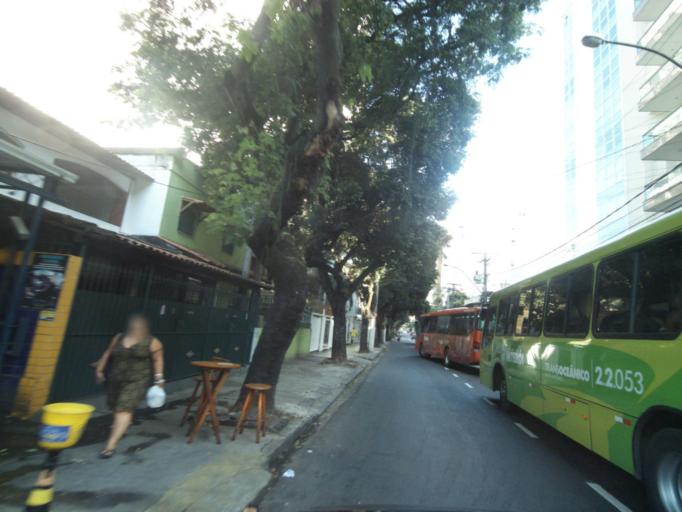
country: BR
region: Rio de Janeiro
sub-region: Niteroi
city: Niteroi
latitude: -22.8996
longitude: -43.1038
